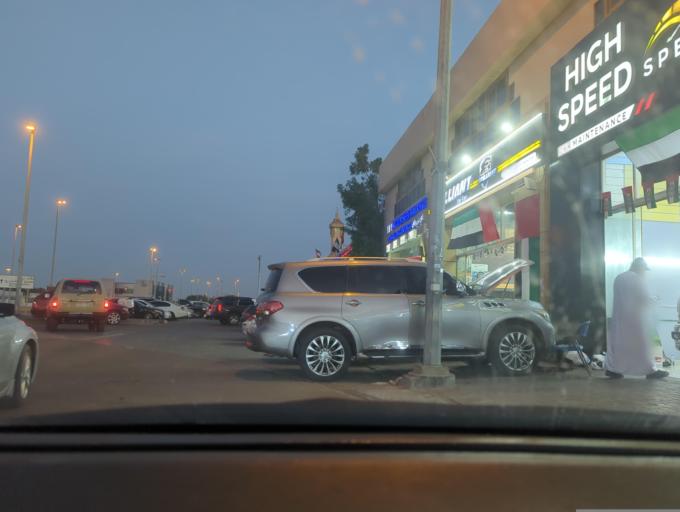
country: AE
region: Abu Dhabi
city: Abu Dhabi
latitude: 24.3778
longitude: 54.5191
